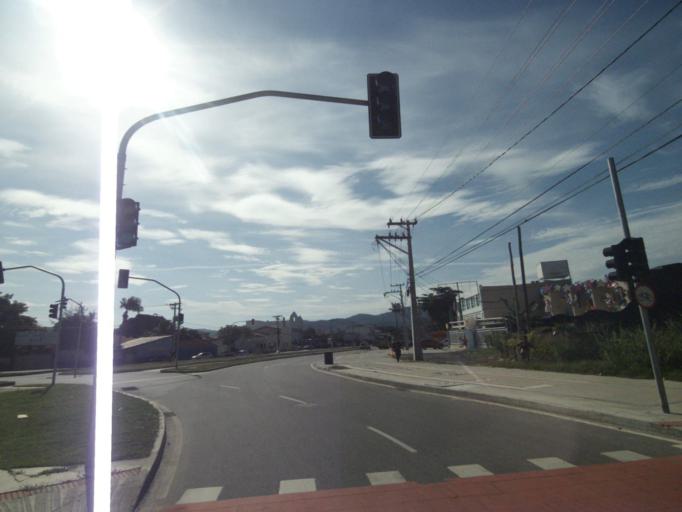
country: BR
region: Rio de Janeiro
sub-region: Niteroi
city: Niteroi
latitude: -22.9530
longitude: -43.0277
